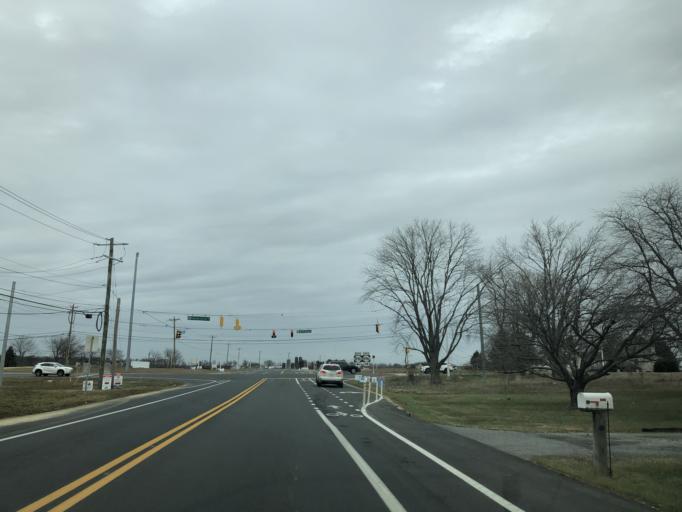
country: US
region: Delaware
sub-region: New Castle County
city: Middletown
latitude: 39.5028
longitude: -75.6848
